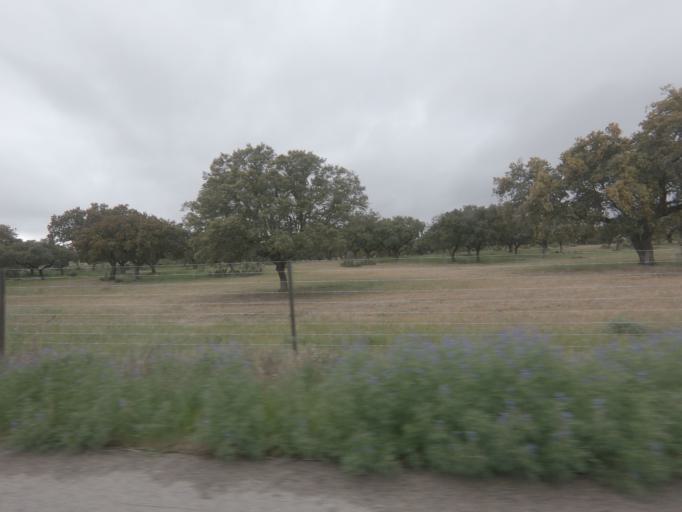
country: ES
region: Extremadura
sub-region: Provincia de Caceres
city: Malpartida de Caceres
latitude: 39.3928
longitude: -6.4284
